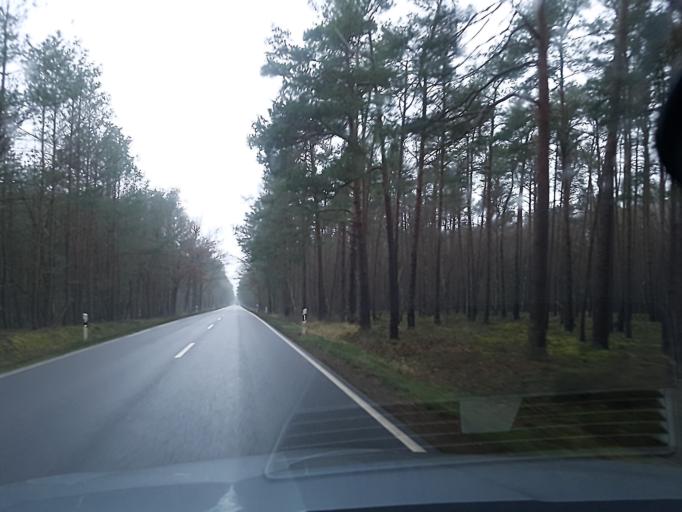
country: DE
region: Brandenburg
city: Schonborn
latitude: 51.6617
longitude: 13.4983
